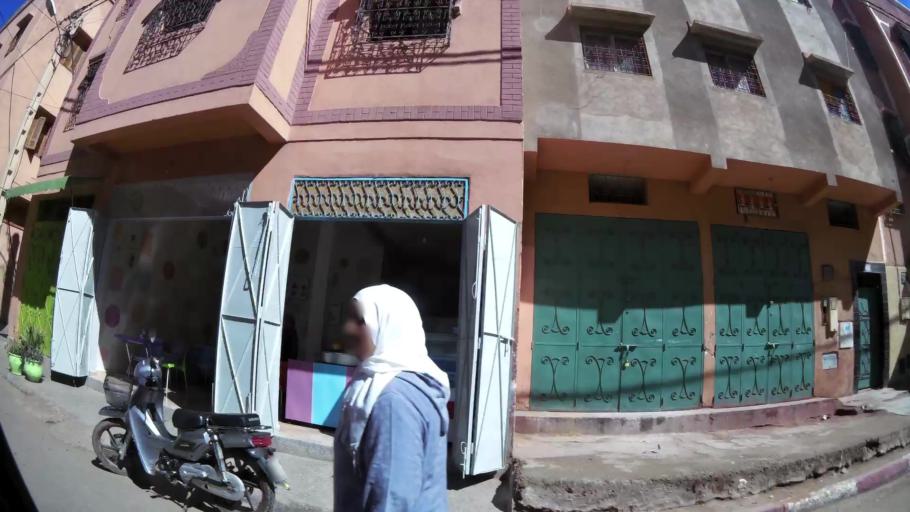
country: MA
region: Marrakech-Tensift-Al Haouz
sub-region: Marrakech
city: Marrakesh
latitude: 31.6461
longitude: -7.9815
